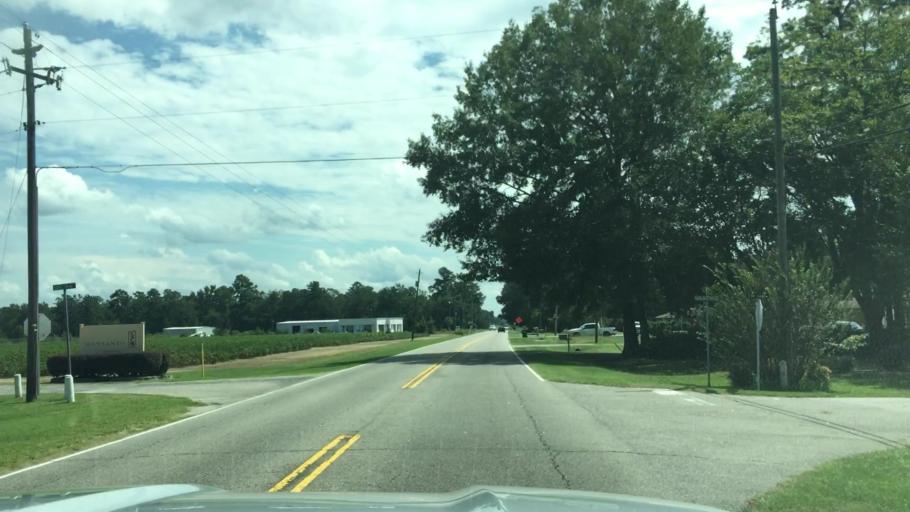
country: US
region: South Carolina
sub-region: Darlington County
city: Hartsville
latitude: 34.3527
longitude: -80.0566
